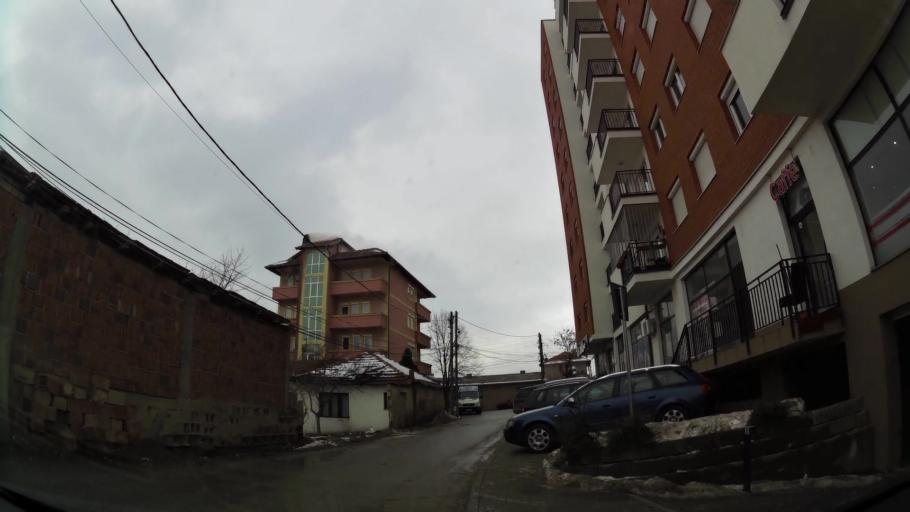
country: XK
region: Pristina
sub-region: Komuna e Prishtines
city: Pristina
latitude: 42.6609
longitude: 21.1739
